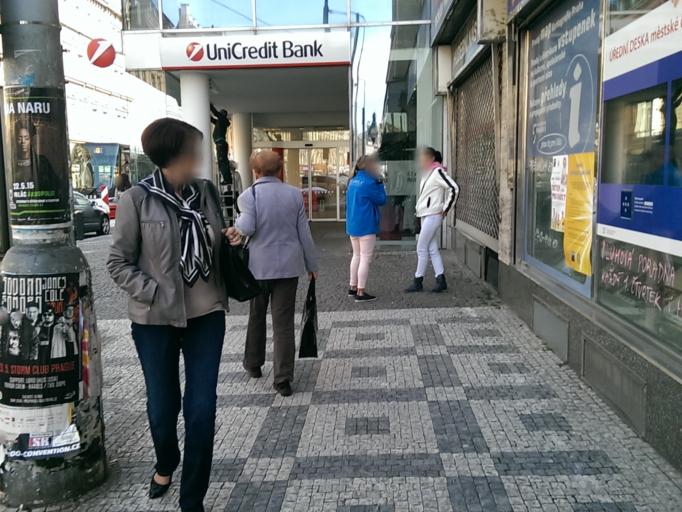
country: CZ
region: Praha
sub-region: Praha 1
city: Mala Strana
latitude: 50.0757
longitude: 14.4043
